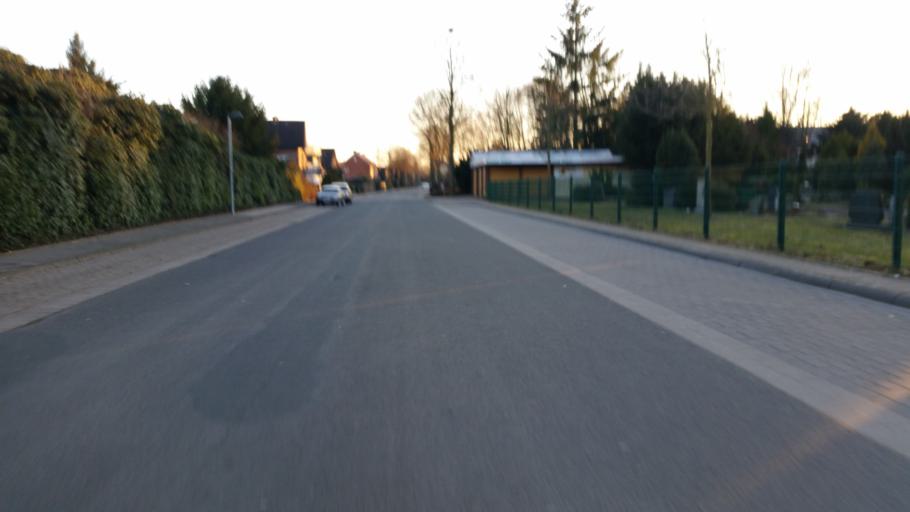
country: DE
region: North Rhine-Westphalia
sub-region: Regierungsbezirk Munster
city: Rheine
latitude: 52.2857
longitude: 7.4092
